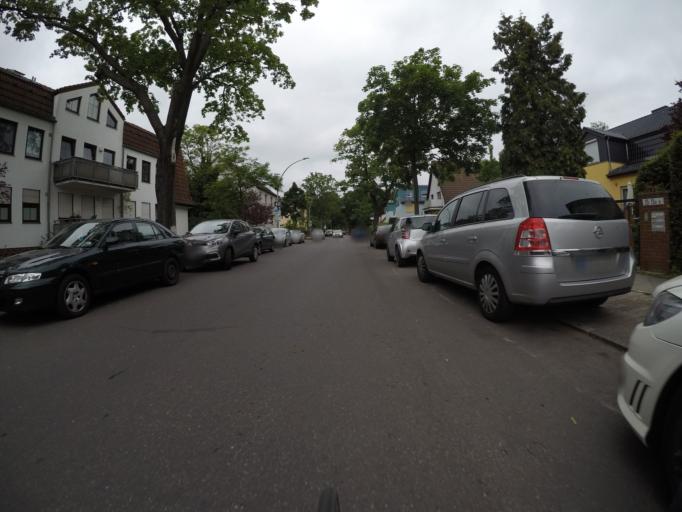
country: DE
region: Berlin
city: Lubars
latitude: 52.6078
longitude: 13.3421
